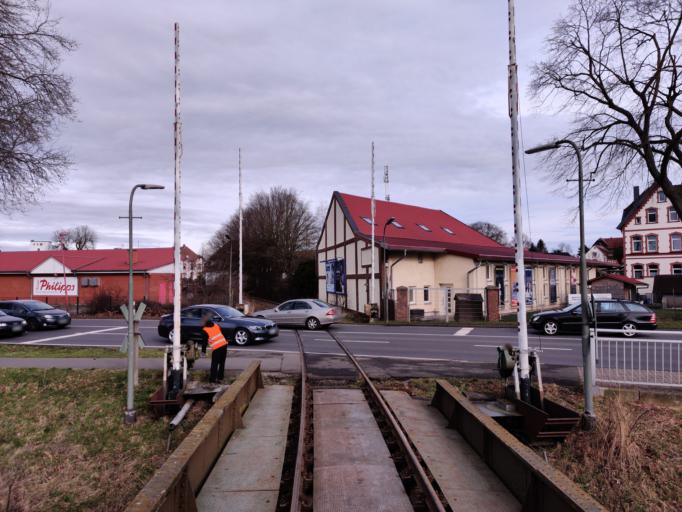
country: DE
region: Lower Saxony
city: Bockenem
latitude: 52.0092
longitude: 10.1236
